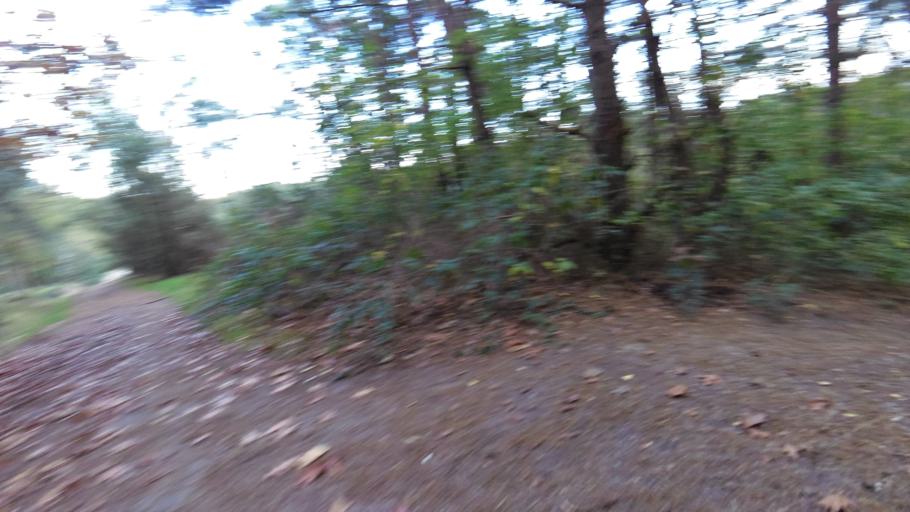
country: NL
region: Gelderland
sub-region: Gemeente Ede
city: Lunteren
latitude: 52.0996
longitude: 5.6569
